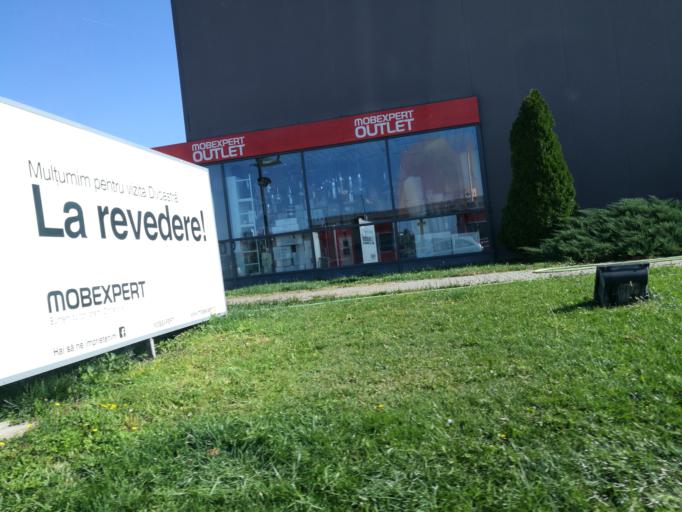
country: RO
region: Ilfov
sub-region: Comuna Chiajna
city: Chiajna
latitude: 44.4379
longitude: 25.9607
